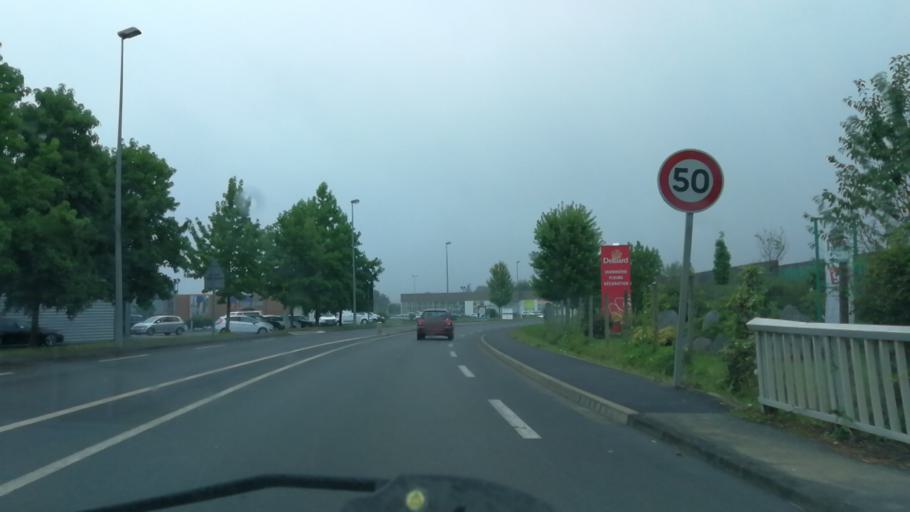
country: FR
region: Aquitaine
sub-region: Departement des Pyrenees-Atlantiques
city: Oloron-Sainte-Marie
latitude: 43.1881
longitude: -0.6247
